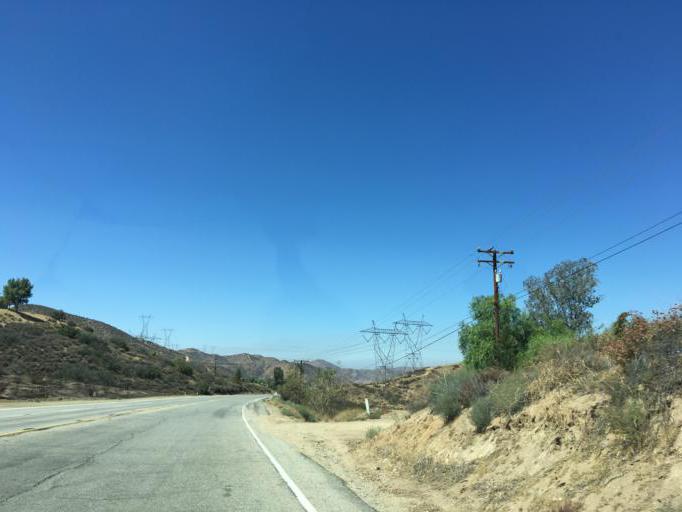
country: US
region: California
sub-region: Los Angeles County
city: Agua Dulce
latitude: 34.5178
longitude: -118.3250
